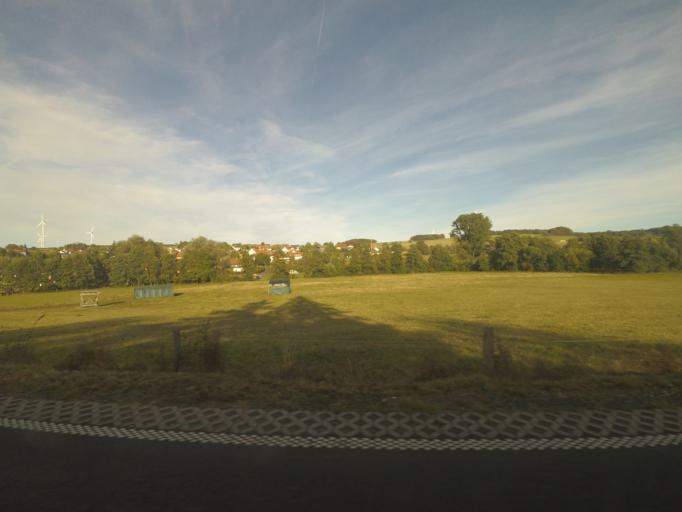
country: DE
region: Hesse
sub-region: Regierungsbezirk Giessen
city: Freiensteinau
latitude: 50.4131
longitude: 9.4616
